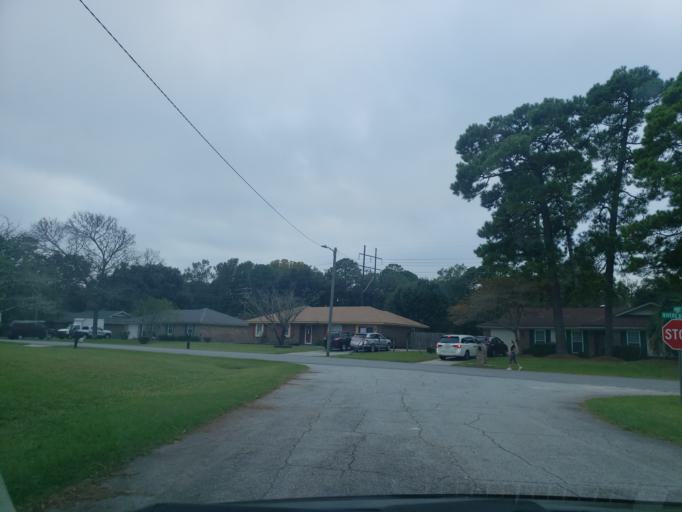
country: US
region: Georgia
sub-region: Chatham County
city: Montgomery
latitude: 31.9505
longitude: -81.1106
